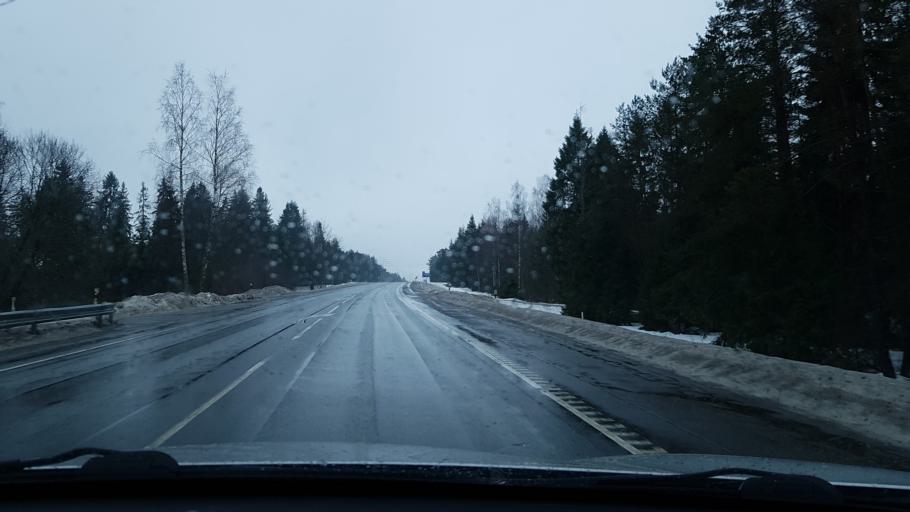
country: EE
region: Raplamaa
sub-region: Kohila vald
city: Kohila
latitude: 59.1869
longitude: 24.7863
